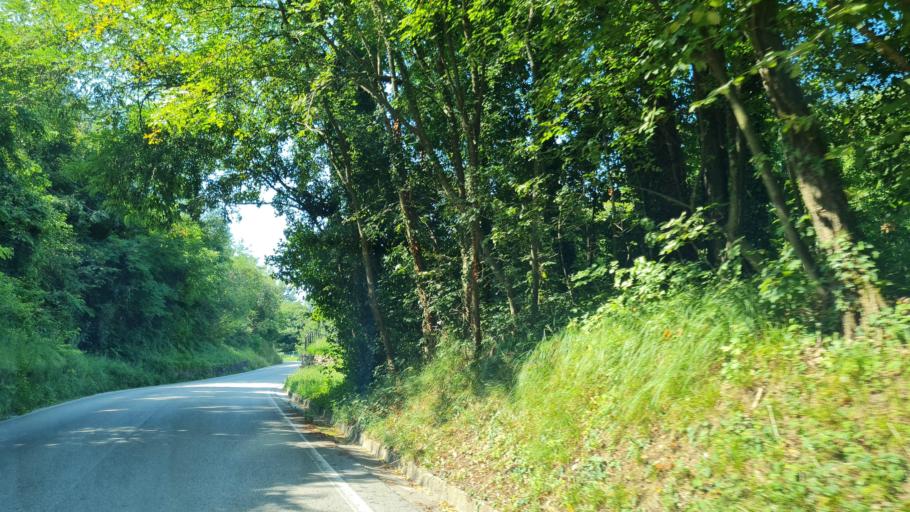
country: IT
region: Veneto
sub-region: Provincia di Vicenza
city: Conco
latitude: 45.7708
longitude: 11.6104
